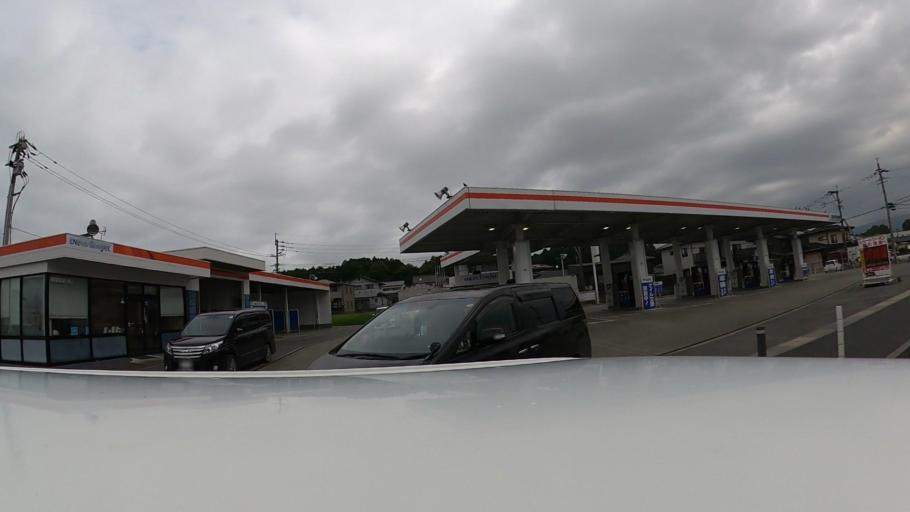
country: JP
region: Kumamoto
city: Ozu
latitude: 32.8372
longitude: 130.8840
